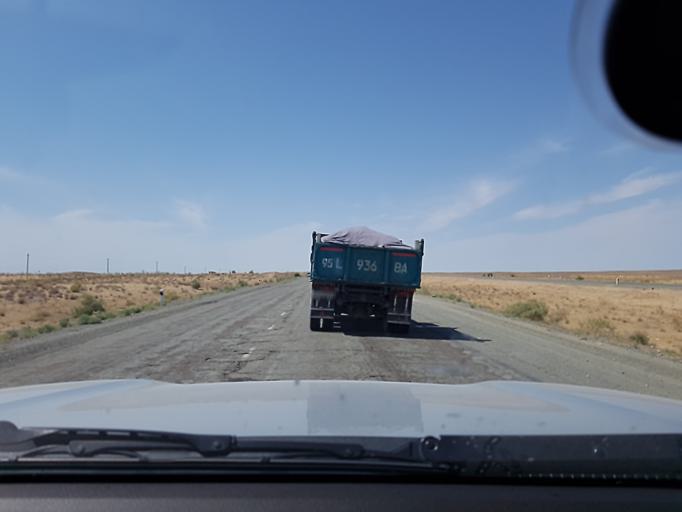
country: UZ
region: Karakalpakstan
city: Mang'it Shahri
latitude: 42.2870
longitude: 60.0785
